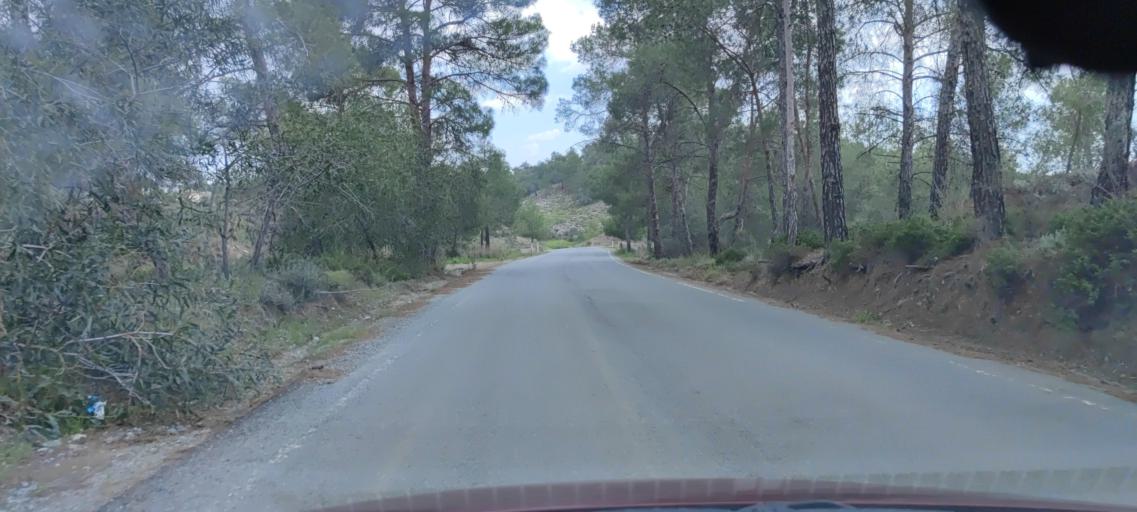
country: CY
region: Larnaka
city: Kornos
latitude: 34.9178
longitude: 33.3570
